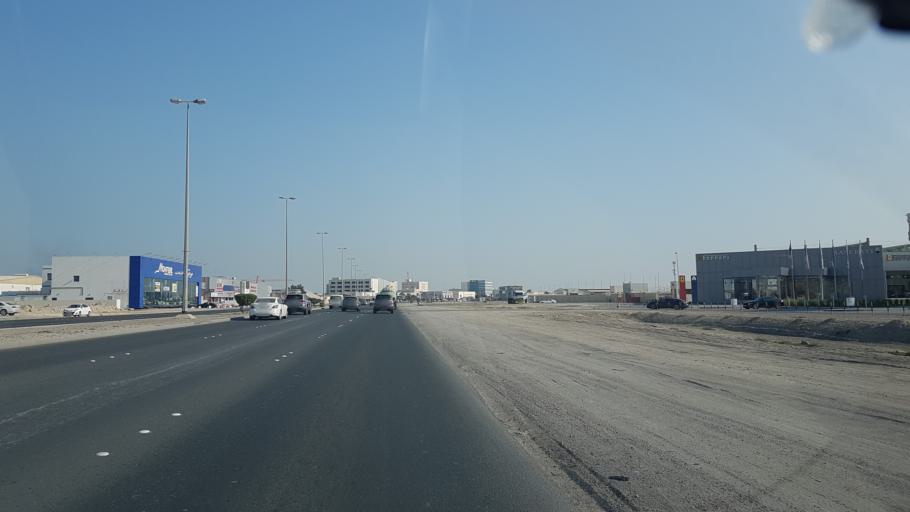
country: BH
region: Northern
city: Sitrah
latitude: 26.1548
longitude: 50.6113
